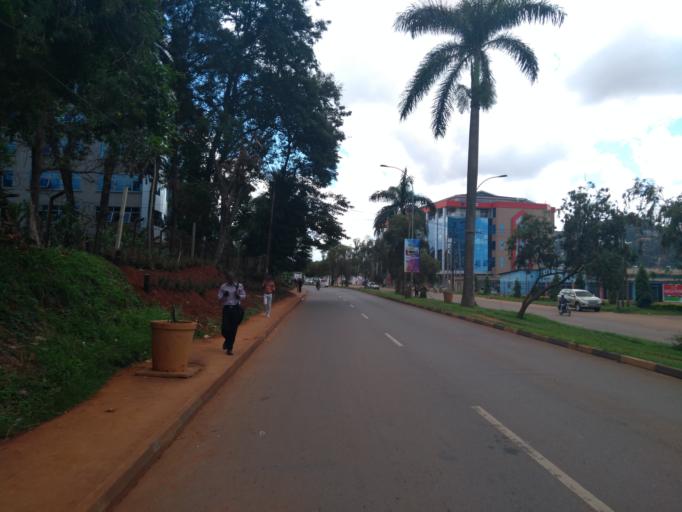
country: UG
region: Central Region
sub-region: Kampala District
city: Kampala
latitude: 0.3338
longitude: 32.6018
